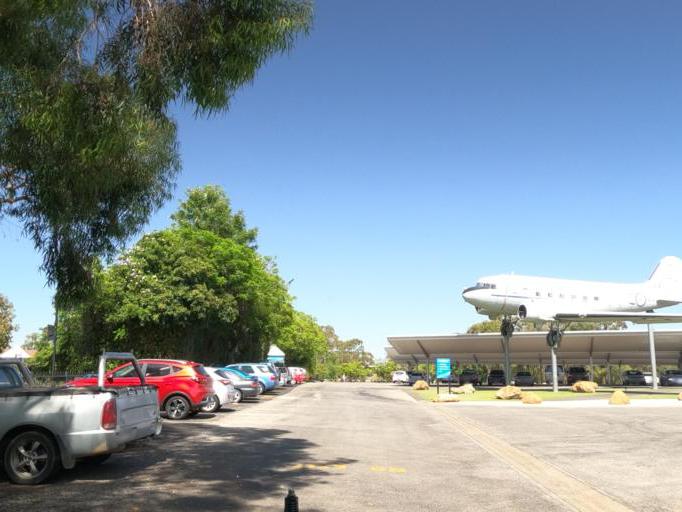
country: AU
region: New South Wales
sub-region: Corowa Shire
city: Mulwala
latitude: -36.0037
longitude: 146.0012
